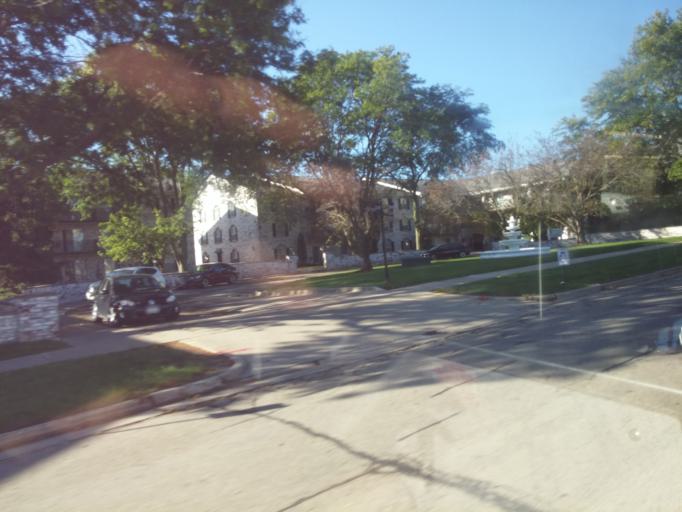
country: US
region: Wisconsin
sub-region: Dane County
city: Shorewood Hills
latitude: 43.0729
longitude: -89.4576
